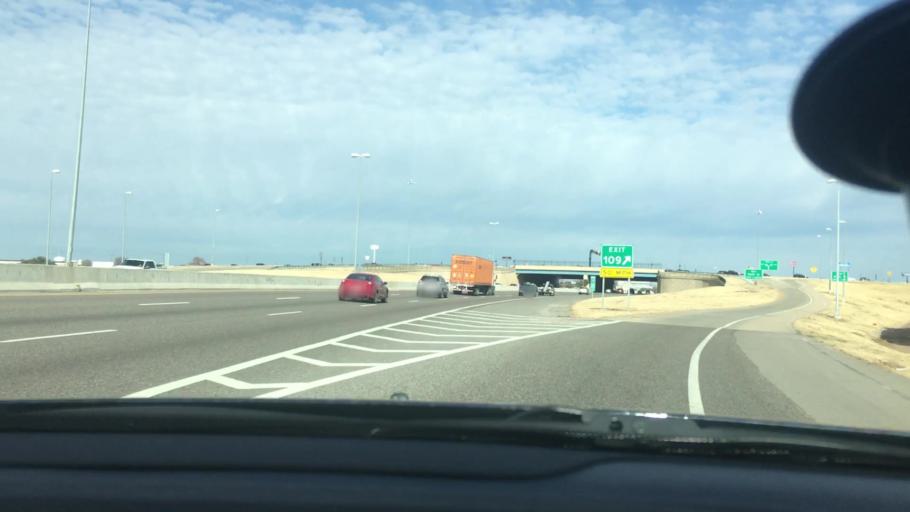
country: US
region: Oklahoma
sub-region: Cleveland County
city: Norman
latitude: 35.2153
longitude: -97.4850
